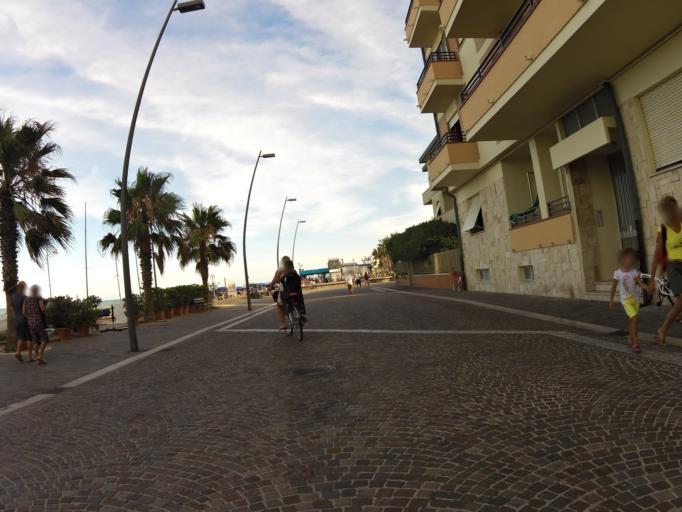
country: IT
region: The Marches
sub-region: Provincia di Macerata
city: Porto Recanati
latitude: 43.4283
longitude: 13.6680
